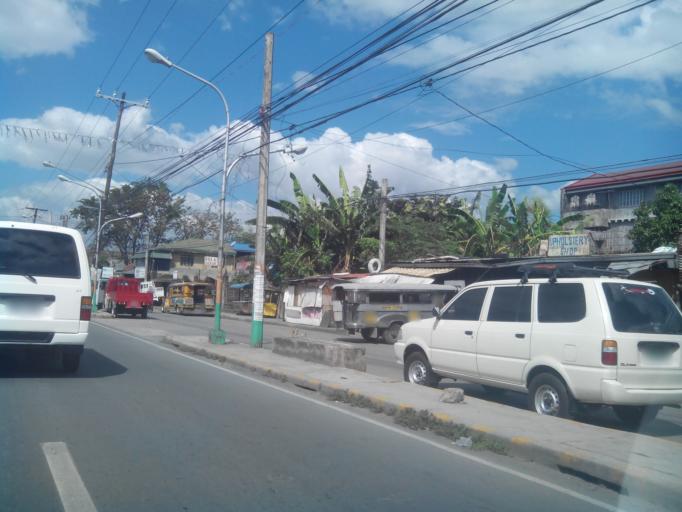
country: PH
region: Calabarzon
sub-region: Province of Rizal
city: Taytay
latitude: 14.5444
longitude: 121.1440
